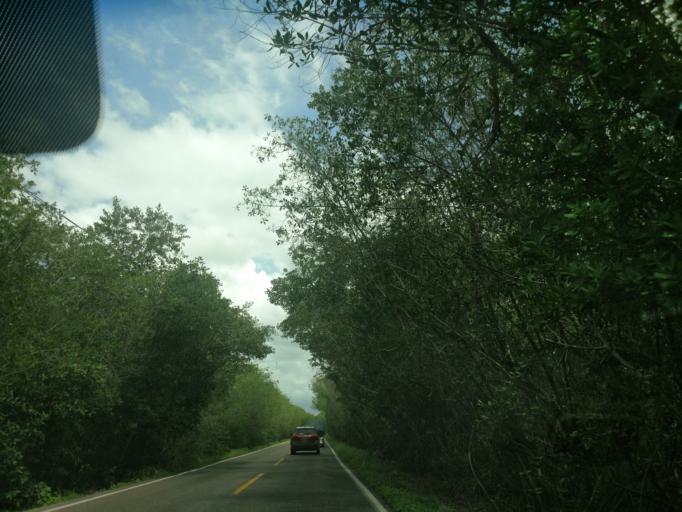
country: MX
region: Nayarit
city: San Blas
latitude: 21.5472
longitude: -105.2531
